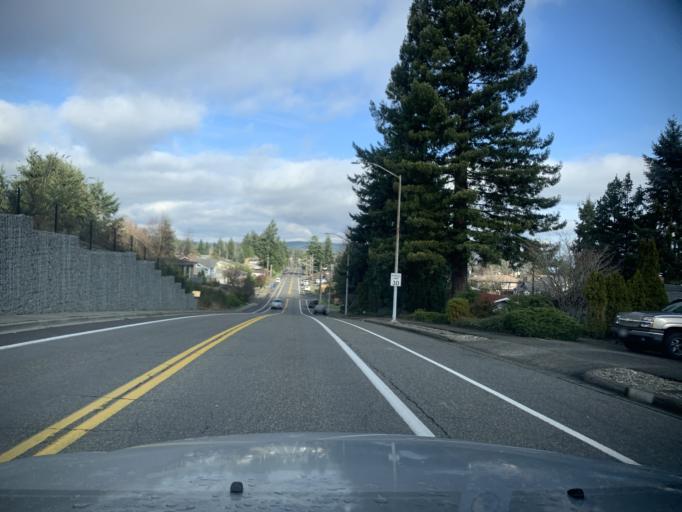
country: US
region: Washington
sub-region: Pierce County
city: Fircrest
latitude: 47.2918
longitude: -122.5210
